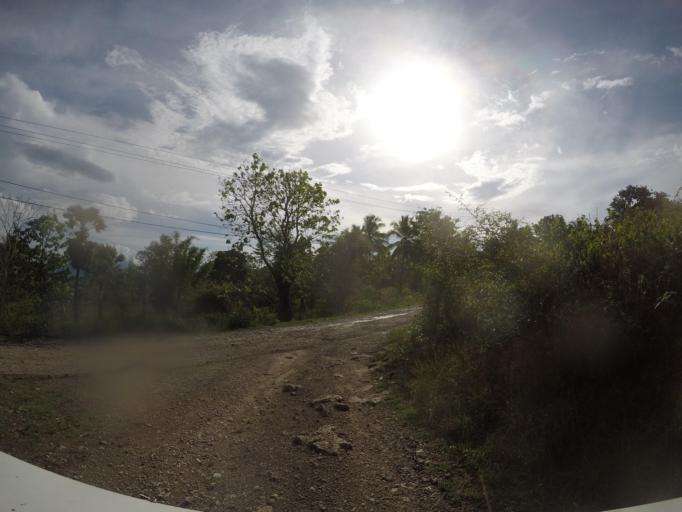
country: TL
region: Baucau
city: Baucau
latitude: -8.5083
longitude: 126.4467
